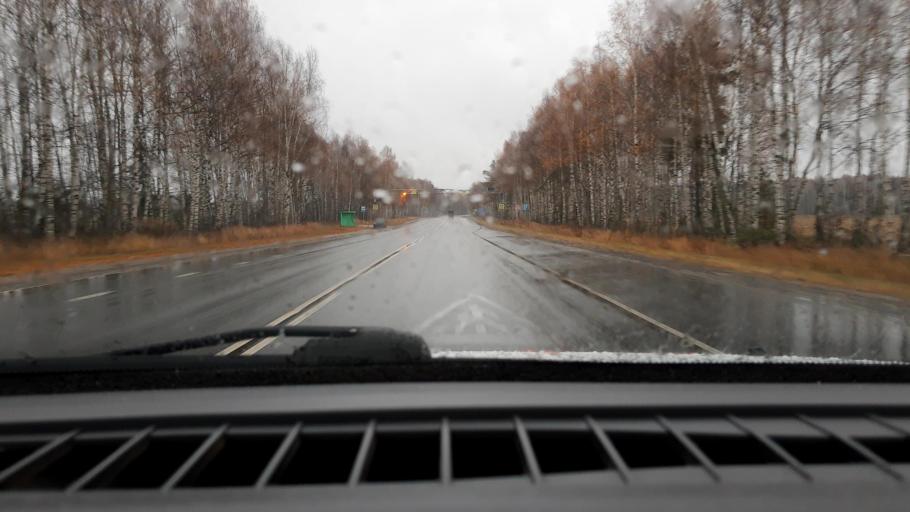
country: RU
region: Nizjnij Novgorod
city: Linda
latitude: 56.6526
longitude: 44.1184
